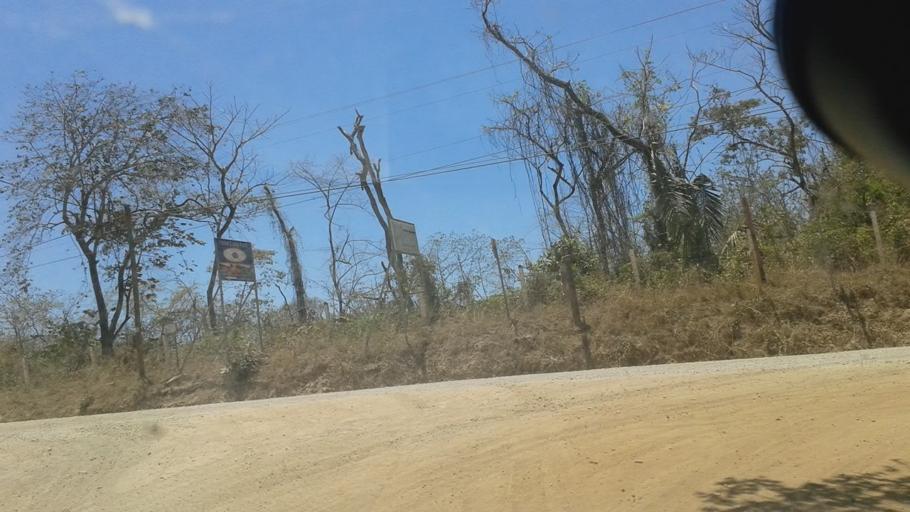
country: CR
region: Guanacaste
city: Samara
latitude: 10.0209
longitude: -85.7209
